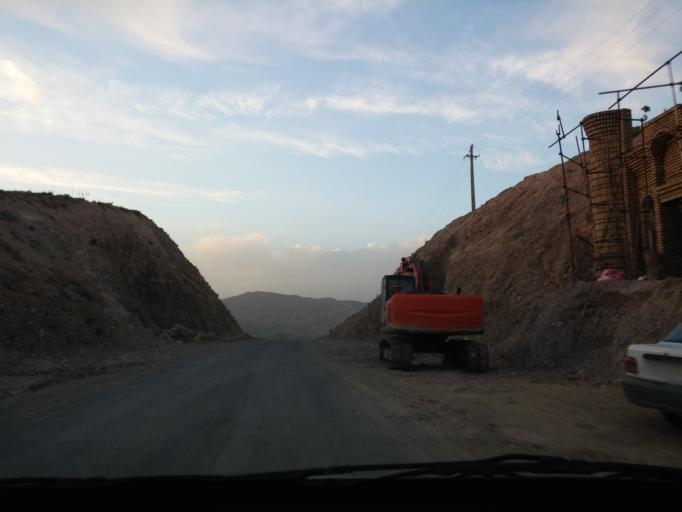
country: IR
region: Semnan
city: Istgah-e Rah Ahan-e Garmsar
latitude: 35.4876
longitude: 52.3325
